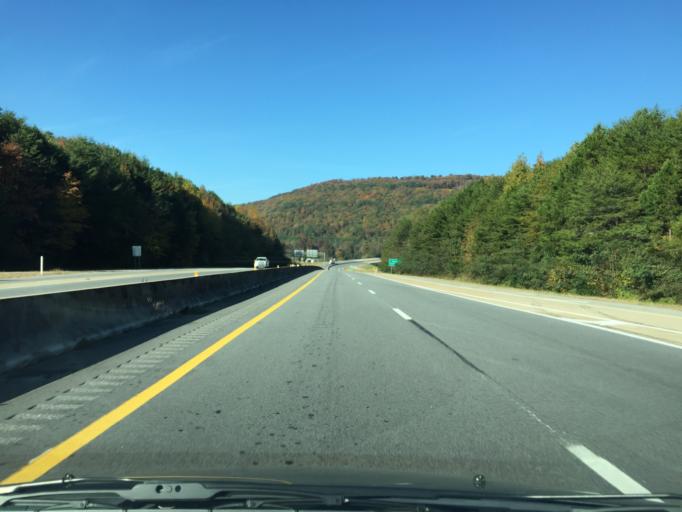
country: US
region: Tennessee
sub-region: Hamilton County
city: Soddy-Daisy
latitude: 35.3036
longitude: -85.1542
